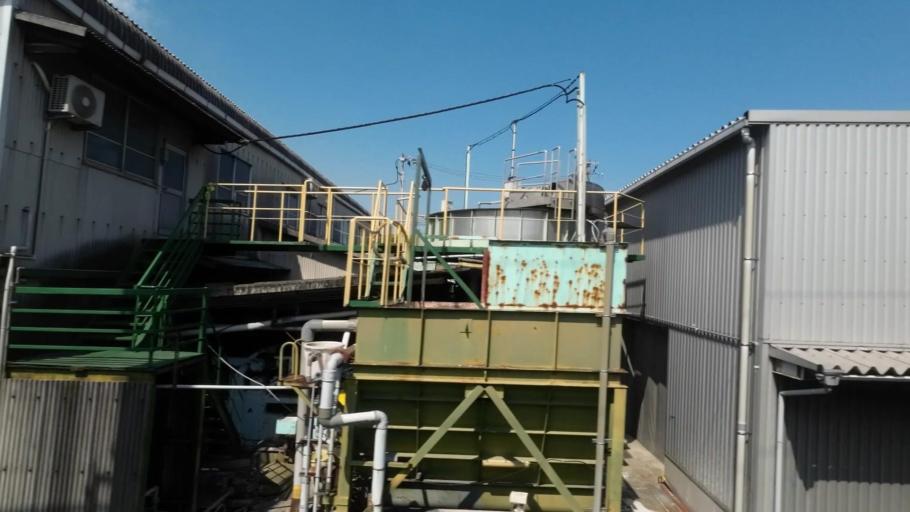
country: JP
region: Ehime
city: Kawanoecho
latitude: 34.0096
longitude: 133.5754
